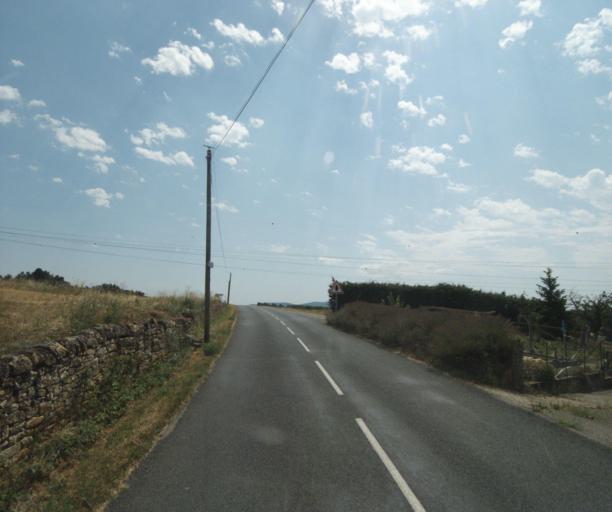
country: FR
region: Rhone-Alpes
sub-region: Departement du Rhone
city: Chatillon
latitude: 45.8699
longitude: 4.6040
